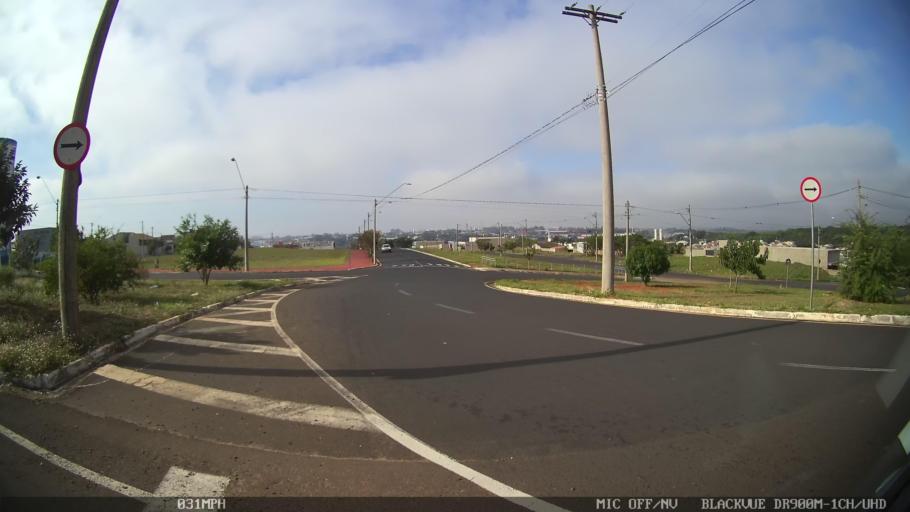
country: BR
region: Sao Paulo
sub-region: Sao Jose Do Rio Preto
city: Sao Jose do Rio Preto
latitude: -20.8007
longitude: -49.4317
